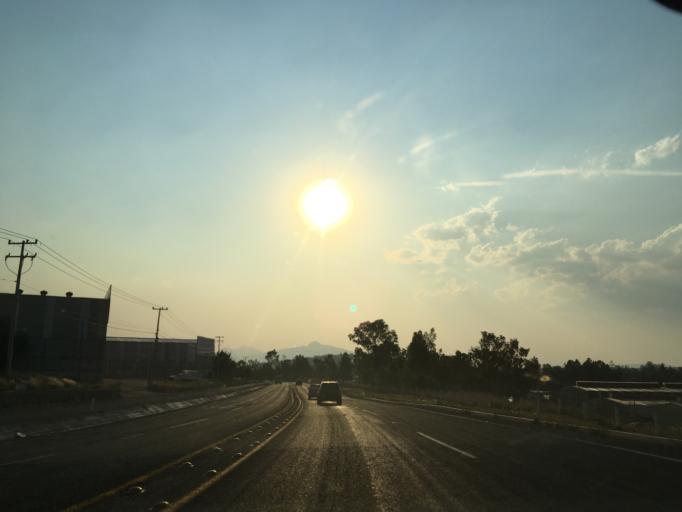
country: MX
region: Michoacan
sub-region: Morelia
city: La Aldea
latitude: 19.7341
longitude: -101.1252
